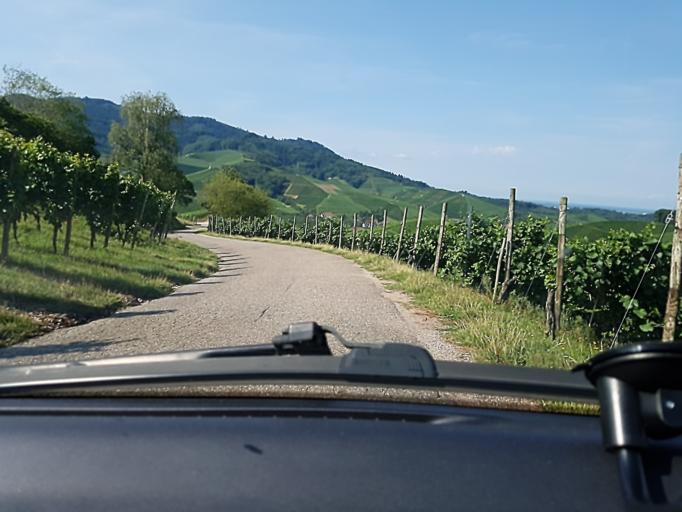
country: DE
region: Baden-Wuerttemberg
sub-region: Freiburg Region
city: Durbach
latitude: 48.5003
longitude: 8.0338
